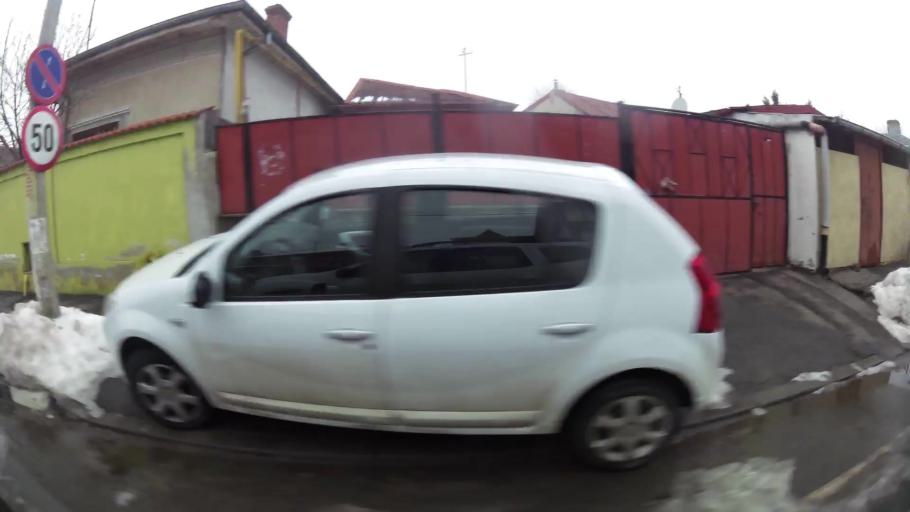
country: RO
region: Ilfov
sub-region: Comuna Chiajna
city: Chiajna
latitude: 44.4612
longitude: 25.9709
